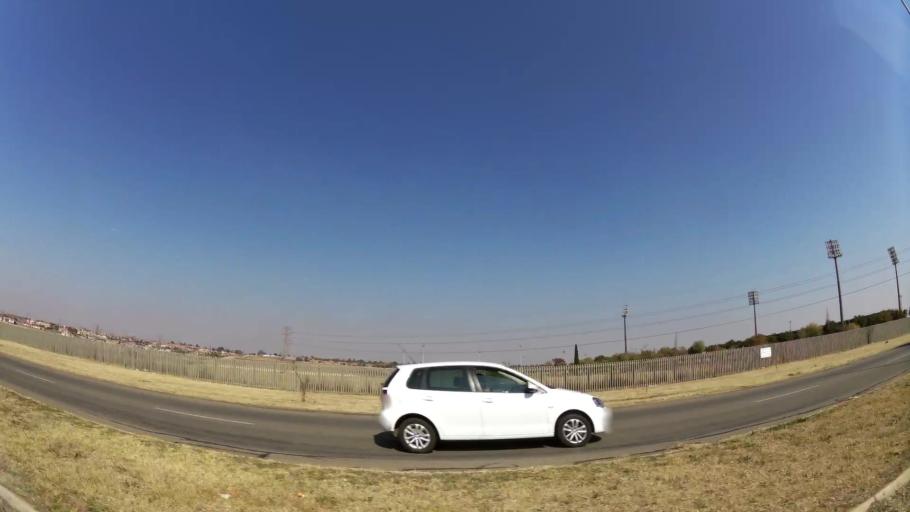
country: ZA
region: Gauteng
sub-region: Ekurhuleni Metropolitan Municipality
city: Boksburg
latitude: -26.2352
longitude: 28.2800
